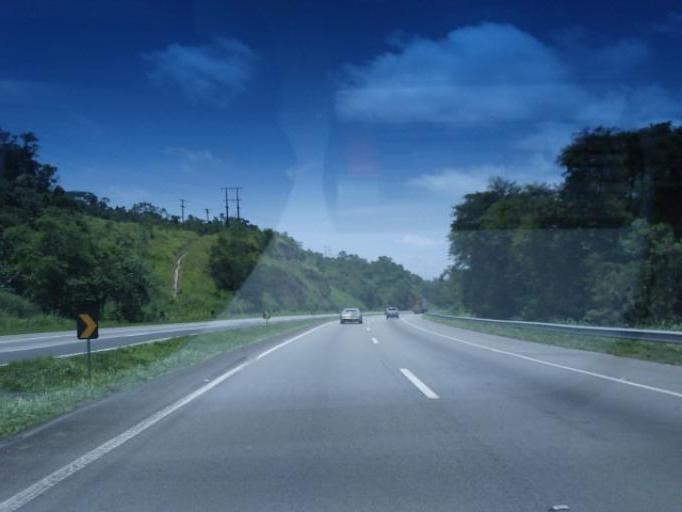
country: BR
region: Sao Paulo
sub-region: Miracatu
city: Miracatu
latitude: -24.3063
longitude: -47.4930
